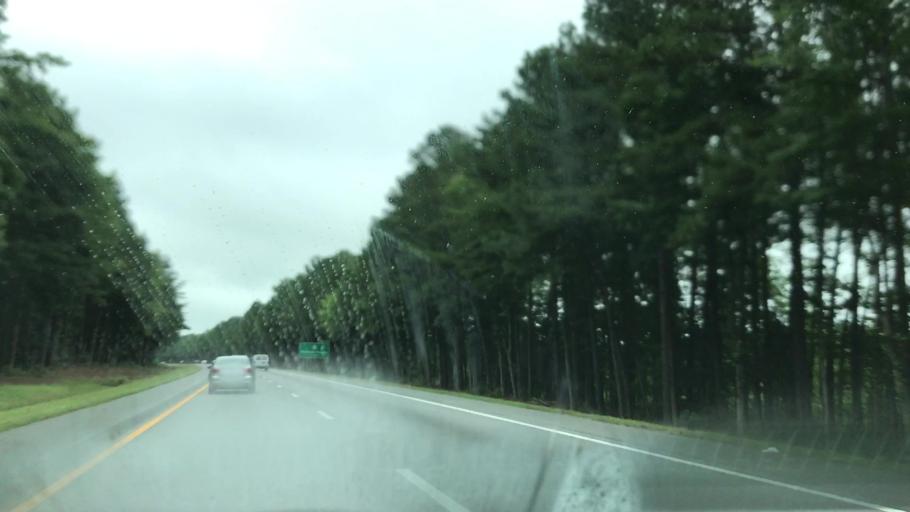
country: US
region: North Carolina
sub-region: Halifax County
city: Weldon
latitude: 36.3882
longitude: -77.6502
